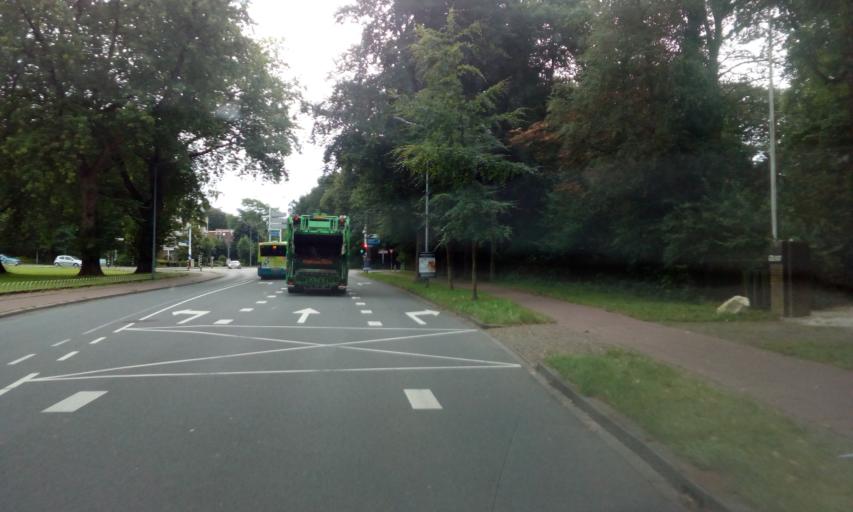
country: NL
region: North Holland
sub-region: Gemeente Hilversum
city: Hilversum
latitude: 52.2329
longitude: 5.1571
